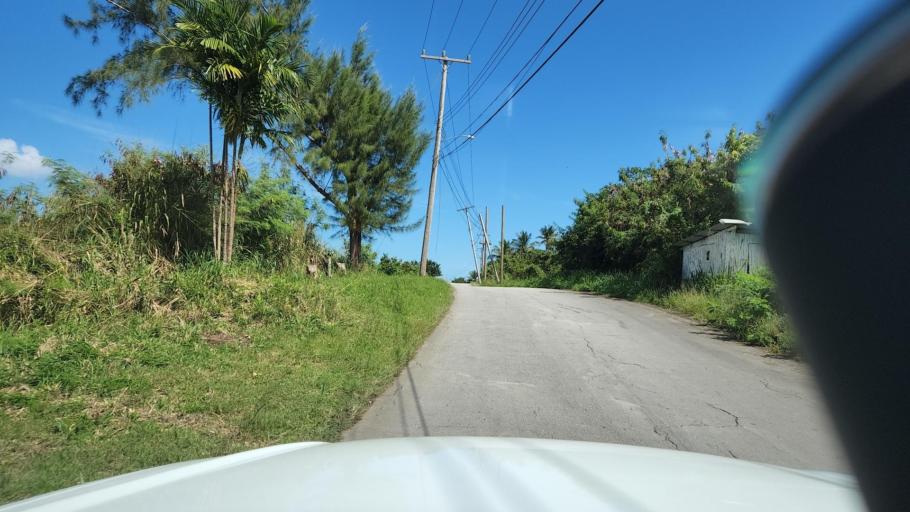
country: BB
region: Saint Joseph
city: Bathsheba
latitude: 13.2109
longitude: -59.5534
